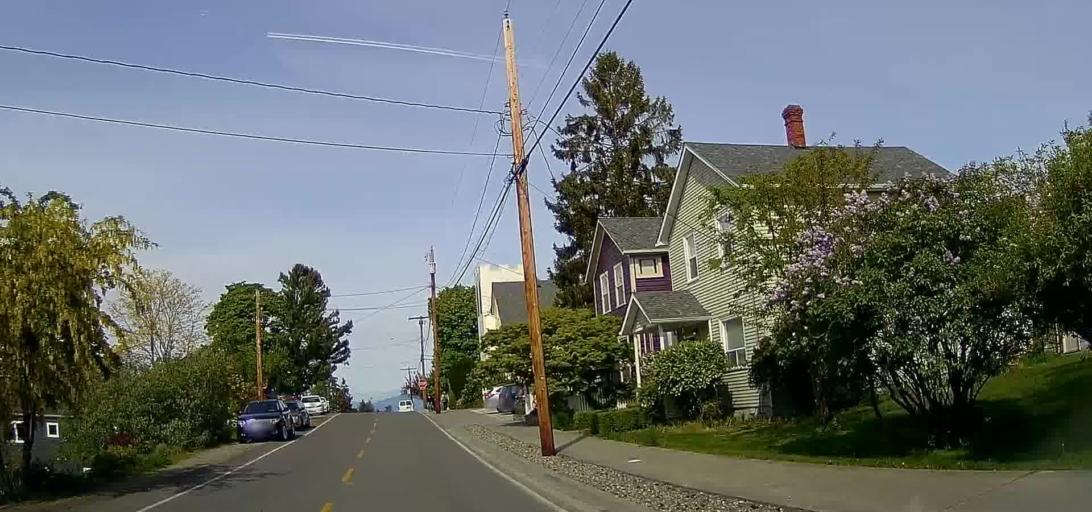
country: US
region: Washington
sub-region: Skagit County
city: Mount Vernon
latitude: 48.3897
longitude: -122.4970
